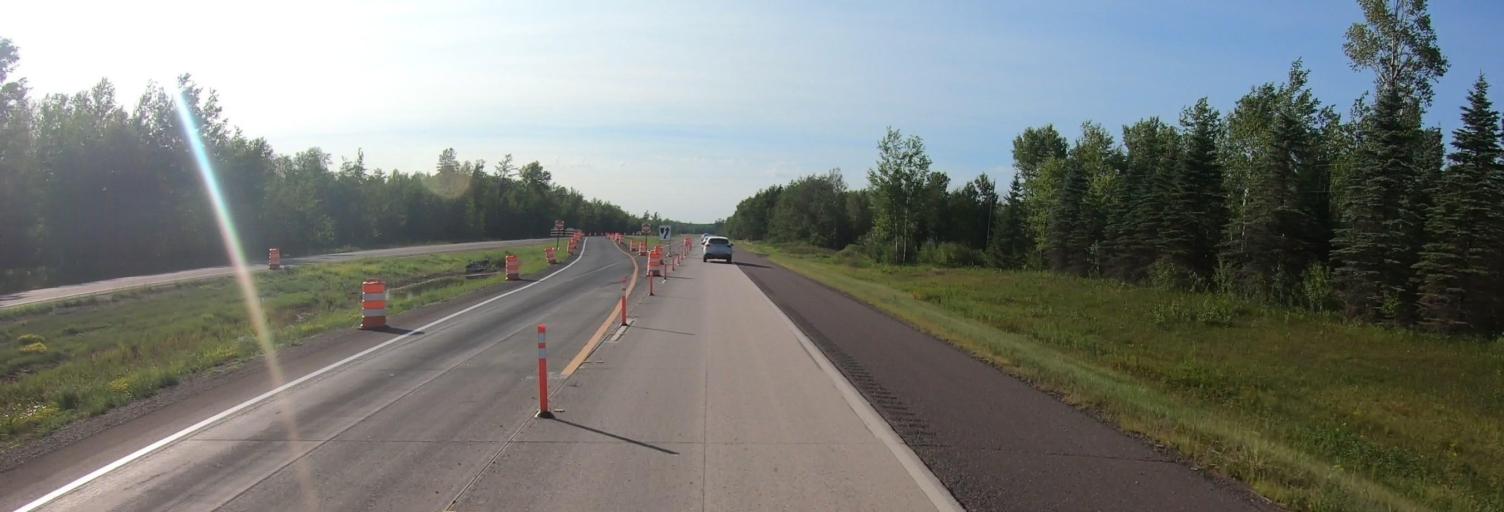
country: US
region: Minnesota
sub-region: Carlton County
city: Cloquet
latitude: 46.9288
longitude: -92.4186
